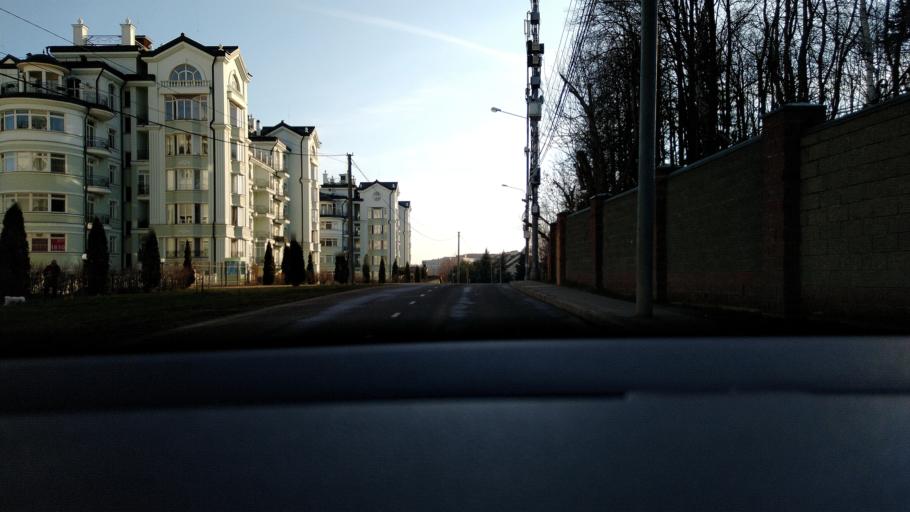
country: RU
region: Moscow
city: Pokrovskoye-Streshnevo
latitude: 55.8299
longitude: 37.4691
